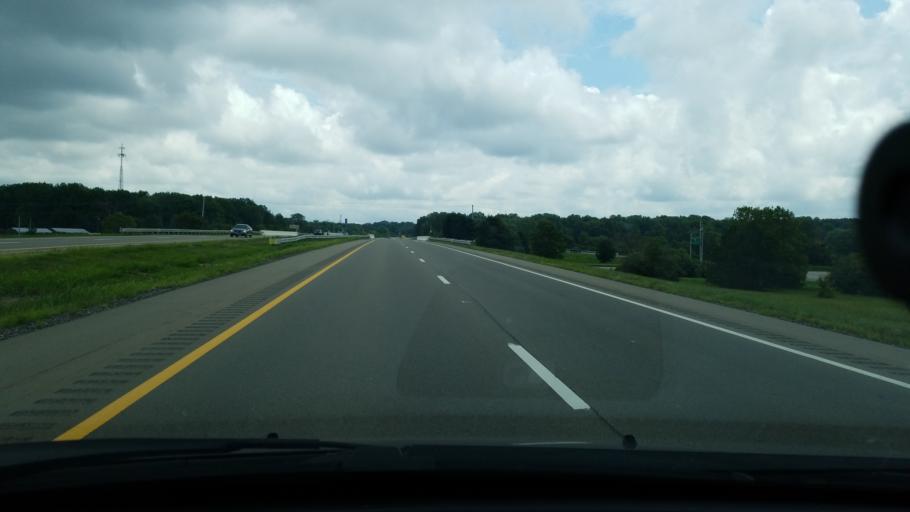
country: US
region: Ohio
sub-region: Lorain County
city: Vermilion-on-the-Lake
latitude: 41.4036
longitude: -82.2849
